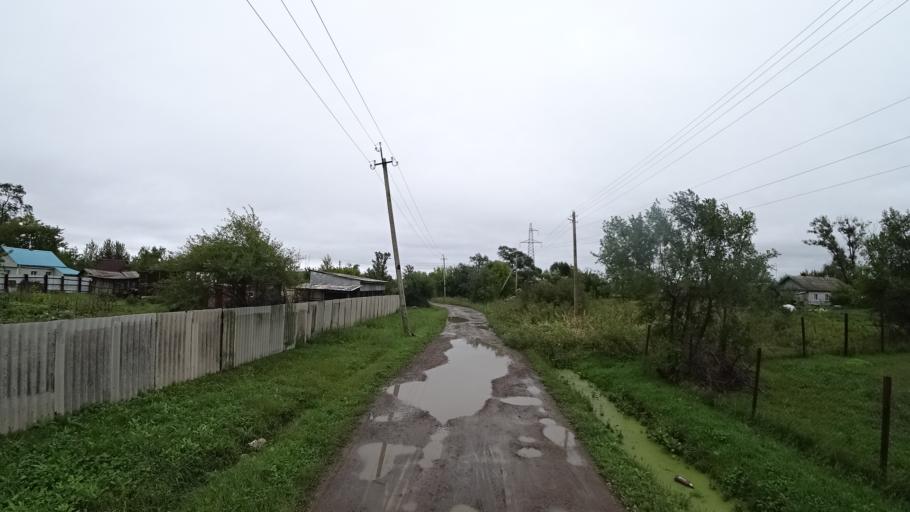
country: RU
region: Primorskiy
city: Monastyrishche
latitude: 44.1967
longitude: 132.4692
